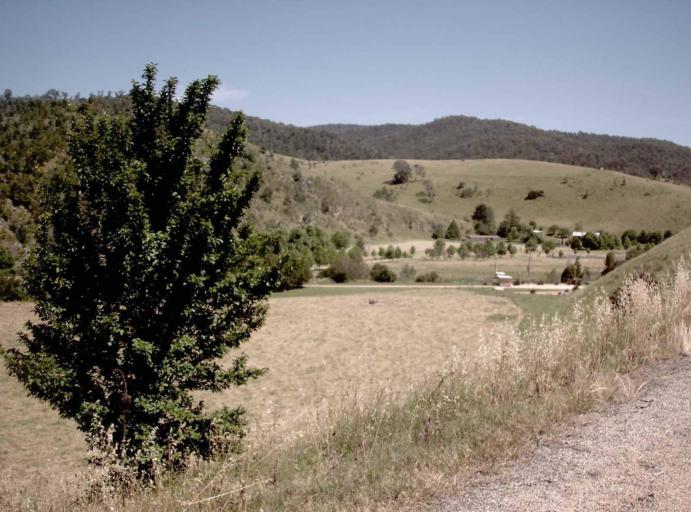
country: AU
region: Victoria
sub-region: East Gippsland
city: Lakes Entrance
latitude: -37.4917
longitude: 148.1726
